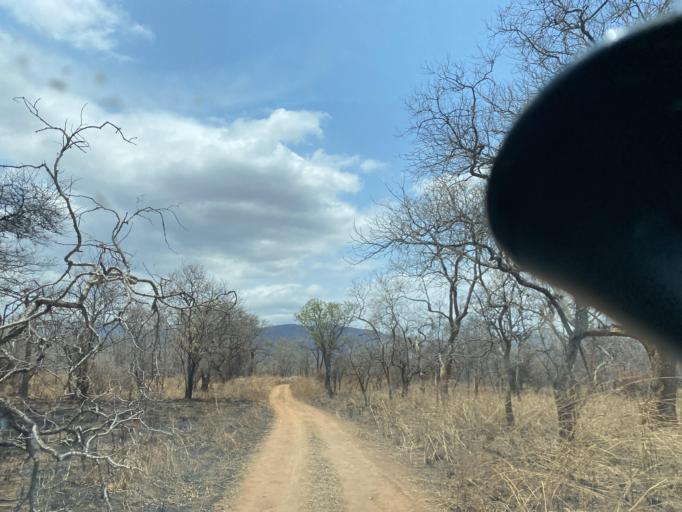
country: ZM
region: Lusaka
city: Luangwa
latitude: -15.1735
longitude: 29.7125
